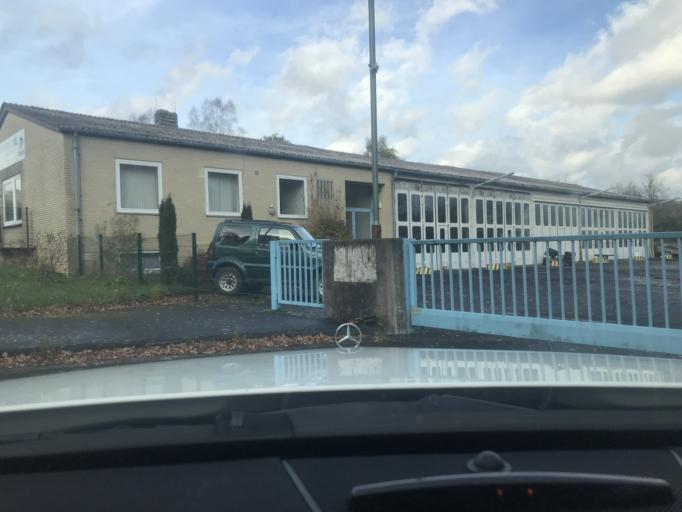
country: DE
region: Thuringia
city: Grossensee
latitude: 50.9367
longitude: 9.9333
